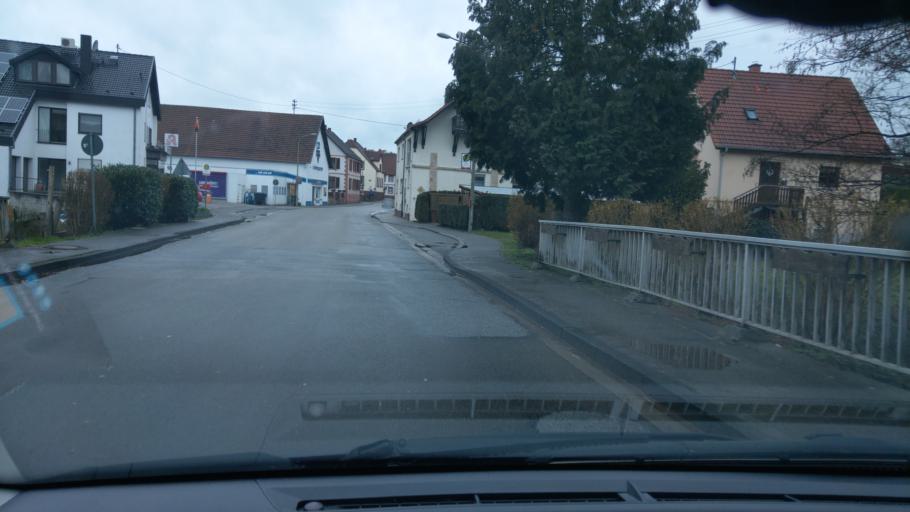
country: DE
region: Rheinland-Pfalz
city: Bechhofen
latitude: 49.3489
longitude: 7.4097
